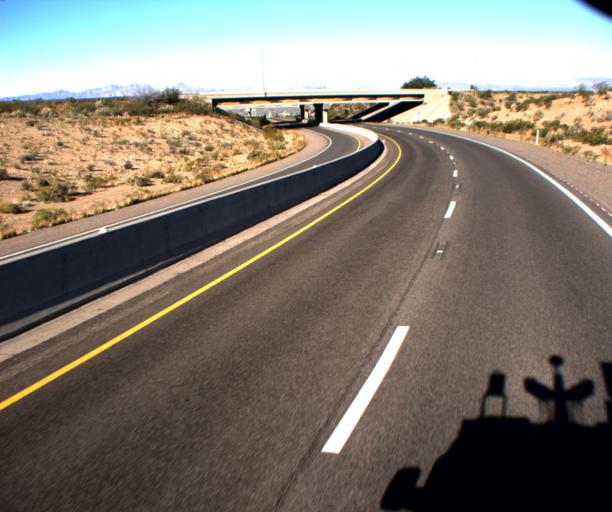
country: US
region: Arizona
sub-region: Mohave County
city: Kingman
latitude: 35.2221
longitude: -114.1241
